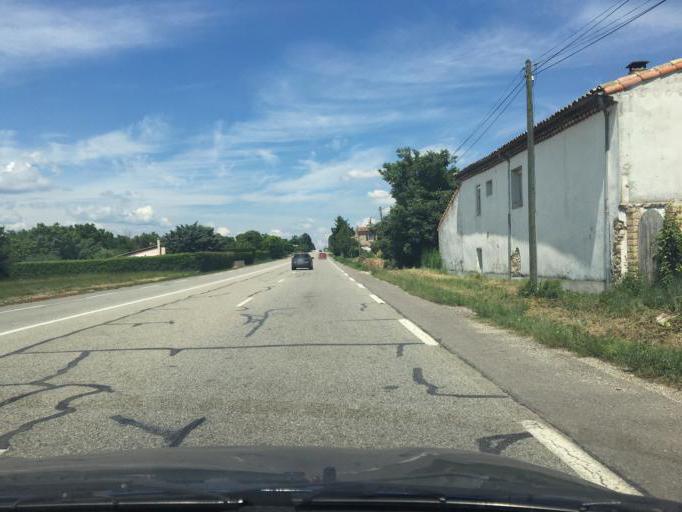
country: FR
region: Rhone-Alpes
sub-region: Departement de la Drome
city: Saulce-sur-Rhone
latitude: 44.7118
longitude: 4.8026
